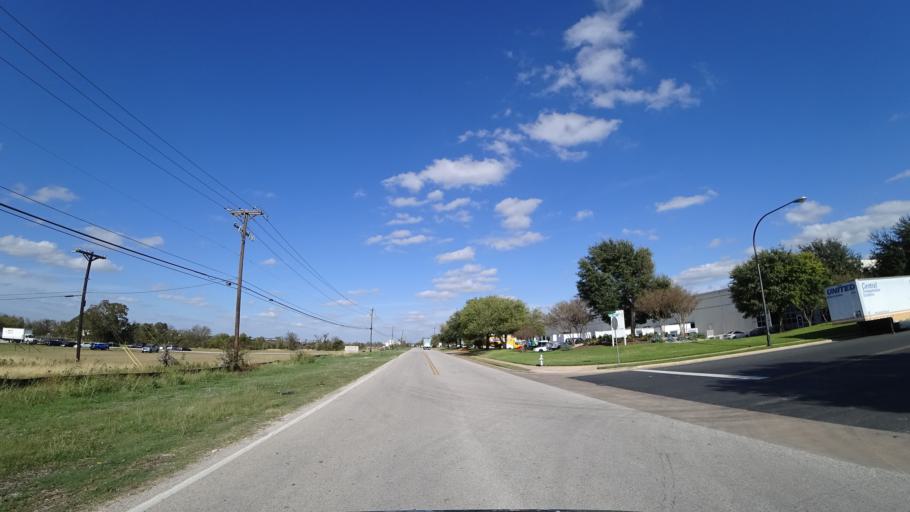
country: US
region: Texas
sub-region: Travis County
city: Wells Branch
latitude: 30.4597
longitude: -97.6763
